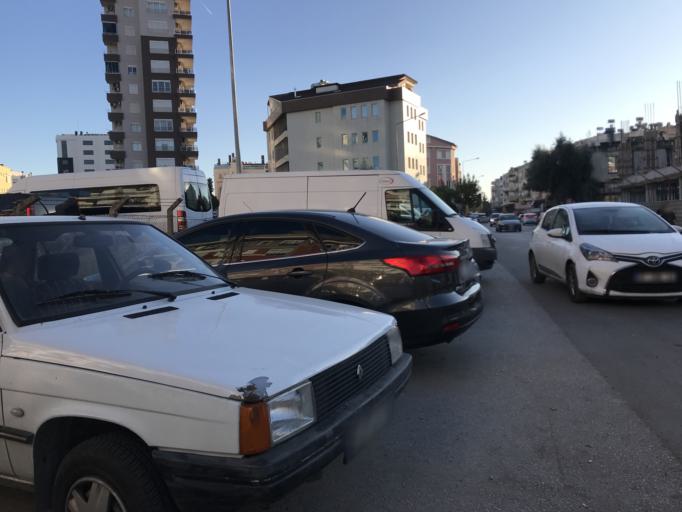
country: TR
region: Antalya
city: Antalya
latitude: 36.8982
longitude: 30.7076
